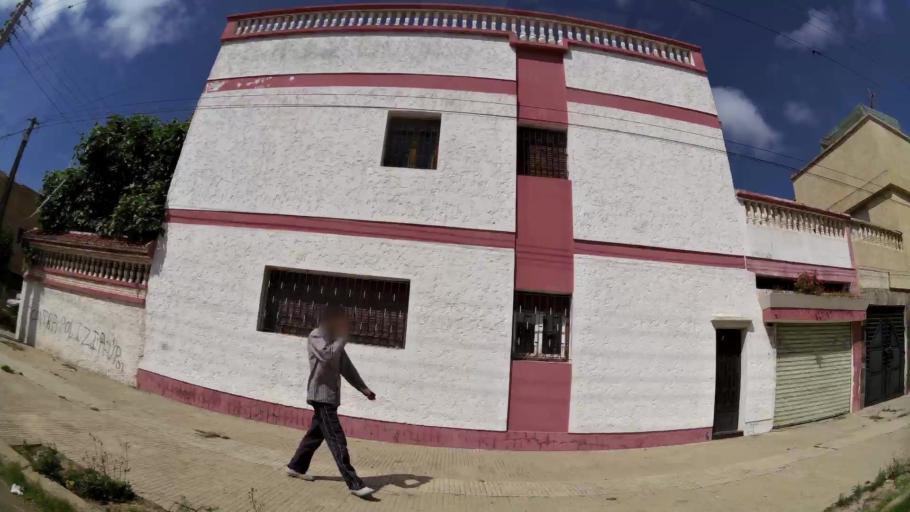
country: MA
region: Rabat-Sale-Zemmour-Zaer
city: Sale
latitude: 34.0397
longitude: -6.7915
